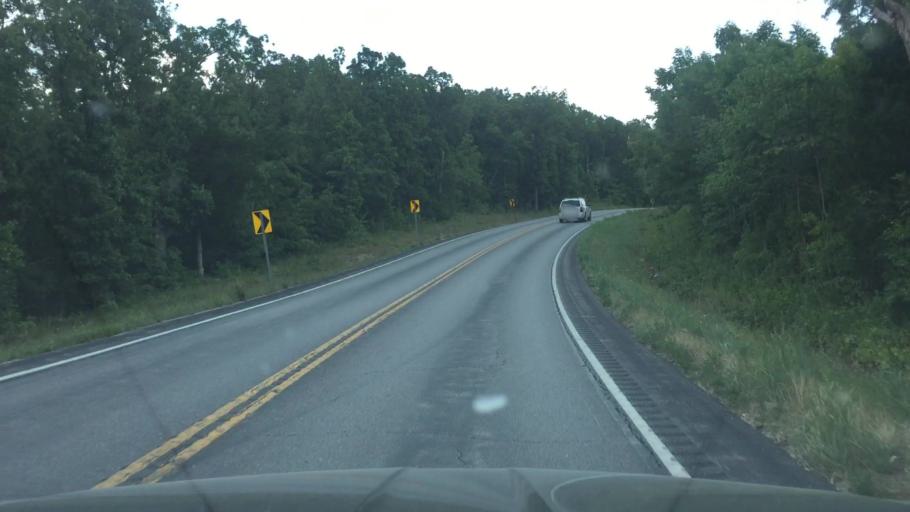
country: US
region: Missouri
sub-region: Miller County
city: Tuscumbia
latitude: 38.0990
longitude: -92.4962
